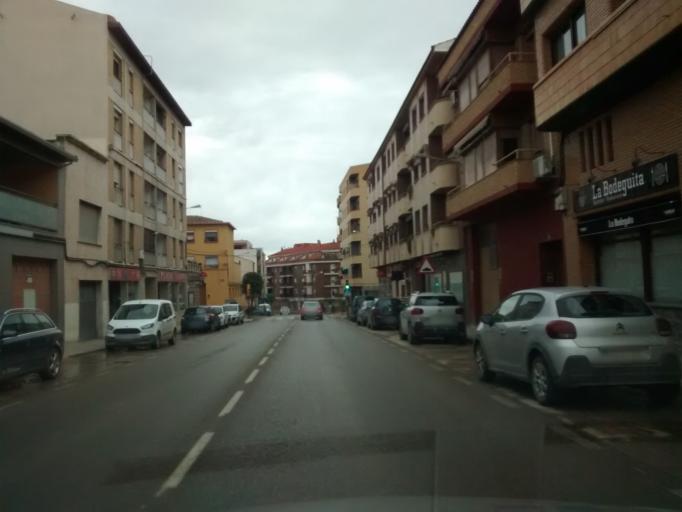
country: ES
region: Aragon
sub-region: Provincia de Zaragoza
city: Caspe
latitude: 41.2338
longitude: -0.0426
